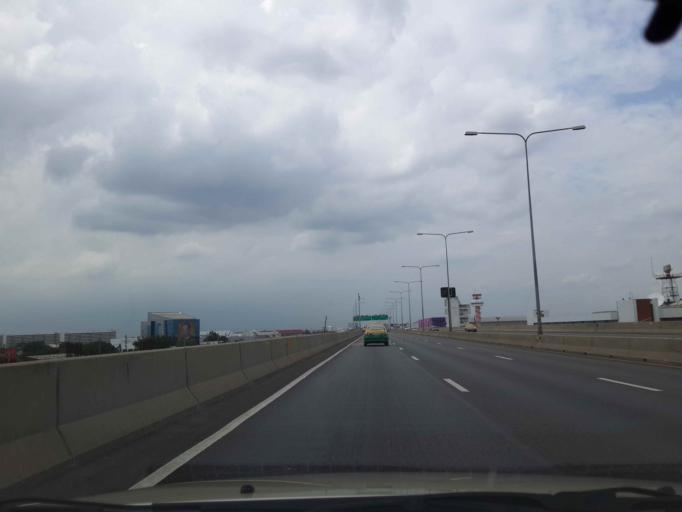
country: TH
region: Bangkok
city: Don Mueang
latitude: 13.9218
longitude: 100.6025
